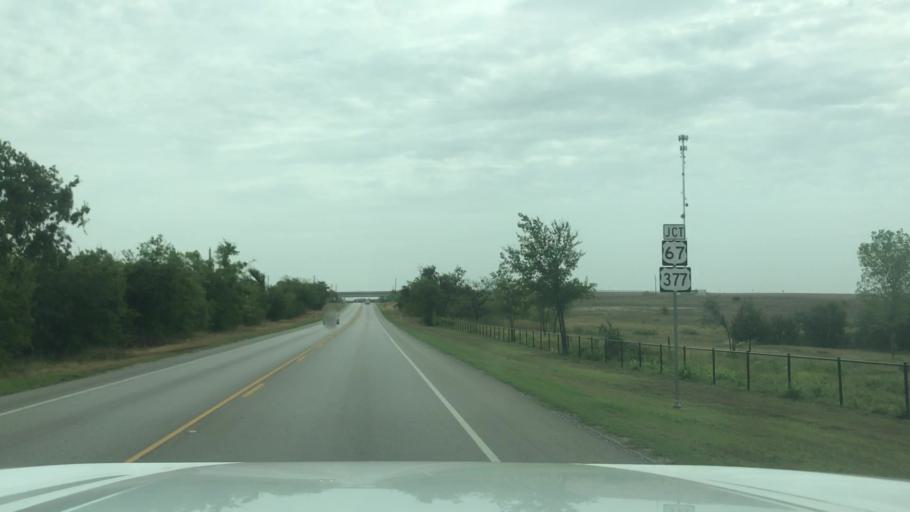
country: US
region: Texas
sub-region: Erath County
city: Dublin
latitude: 32.0949
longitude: -98.3739
